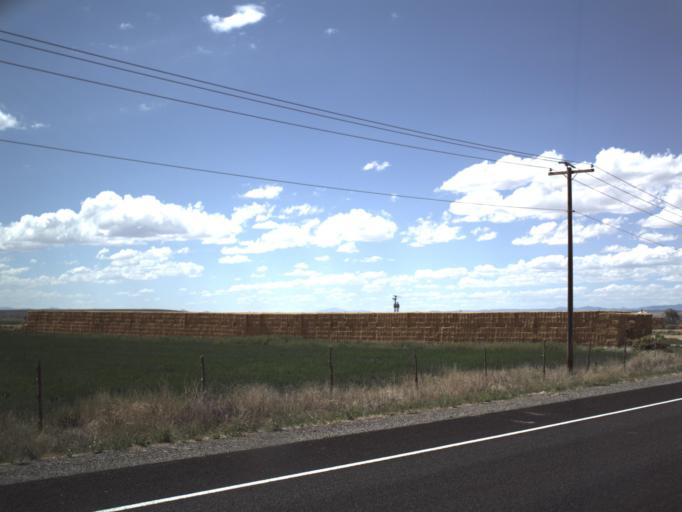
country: US
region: Utah
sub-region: Millard County
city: Fillmore
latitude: 39.1181
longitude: -112.3381
